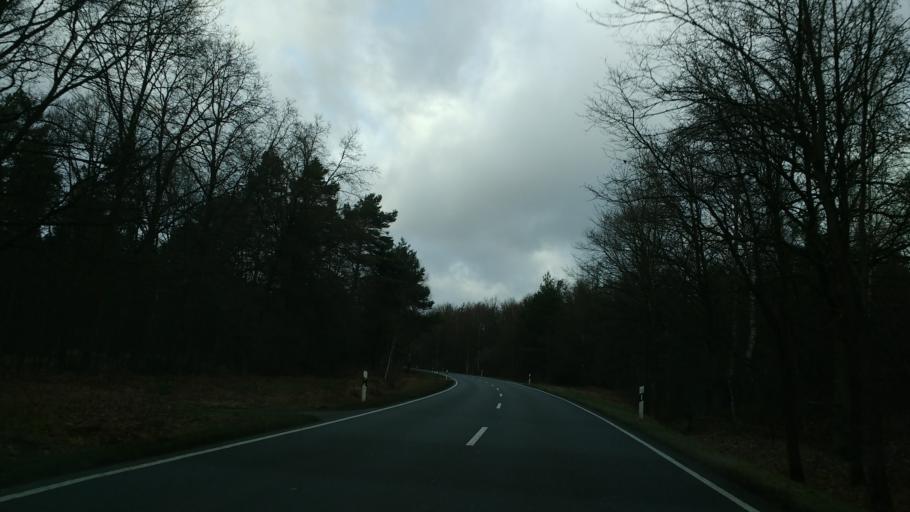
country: DE
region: Lower Saxony
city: Hambuhren
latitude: 52.6137
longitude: 9.9306
